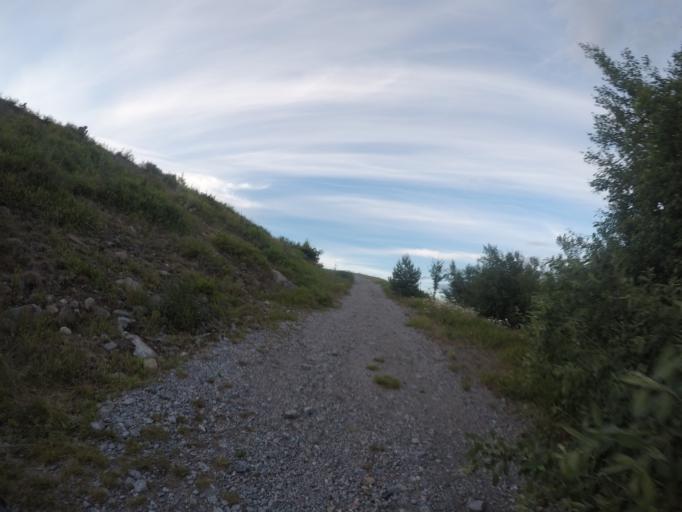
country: SE
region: Stockholm
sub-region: Sigtuna Kommun
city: Rosersberg
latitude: 59.6533
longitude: 17.9576
